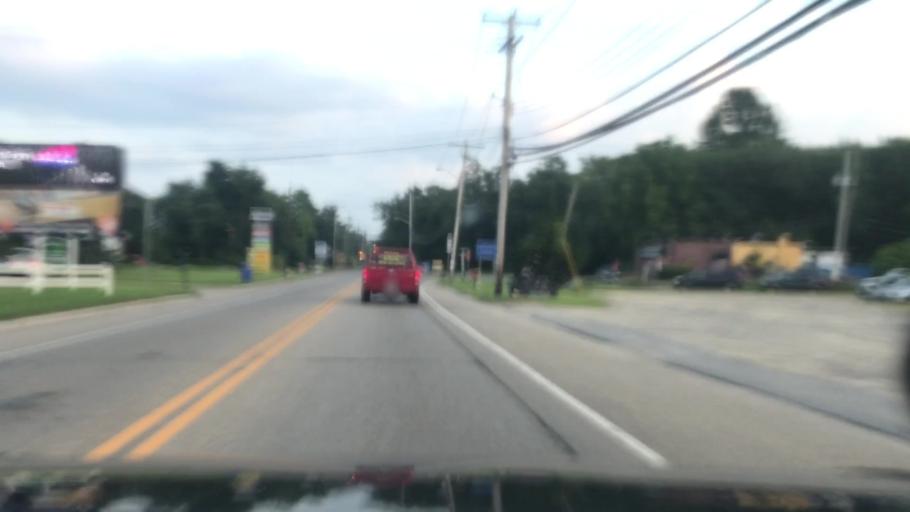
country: US
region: New Jersey
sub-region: Ocean County
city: Pine Lake Park
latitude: 40.0059
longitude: -74.2147
